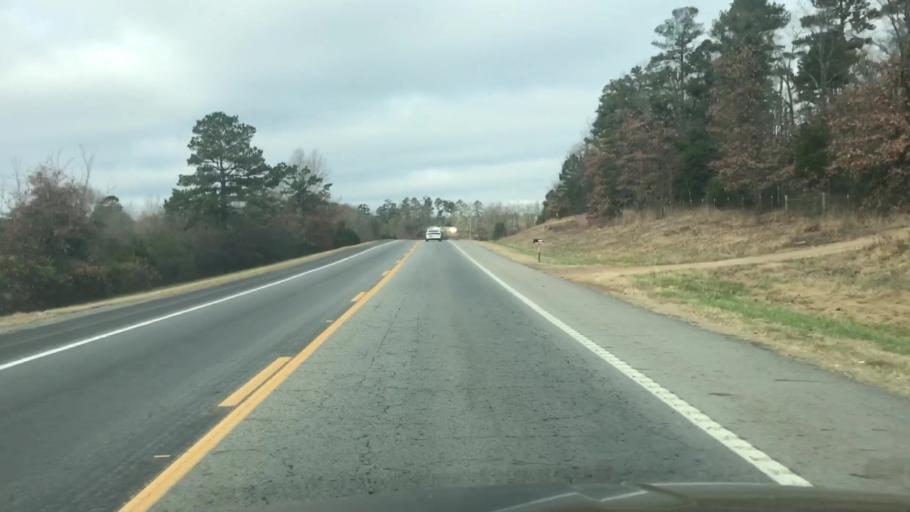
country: US
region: Arkansas
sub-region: Scott County
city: Waldron
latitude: 34.8388
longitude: -94.0501
